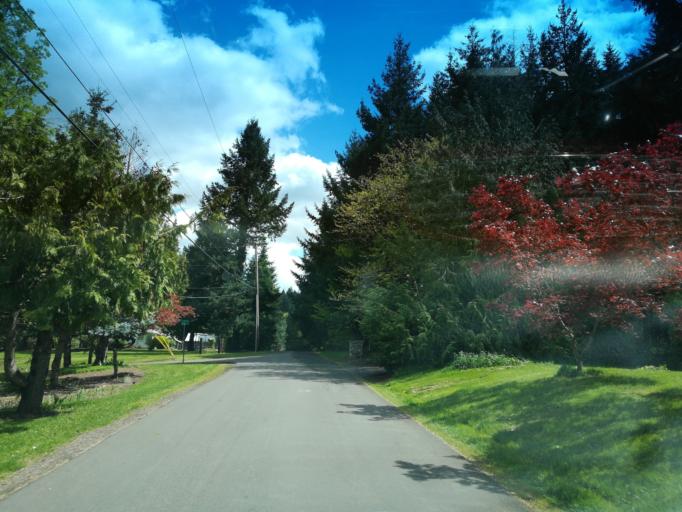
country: US
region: Oregon
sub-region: Clackamas County
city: Damascus
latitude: 45.4278
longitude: -122.4591
